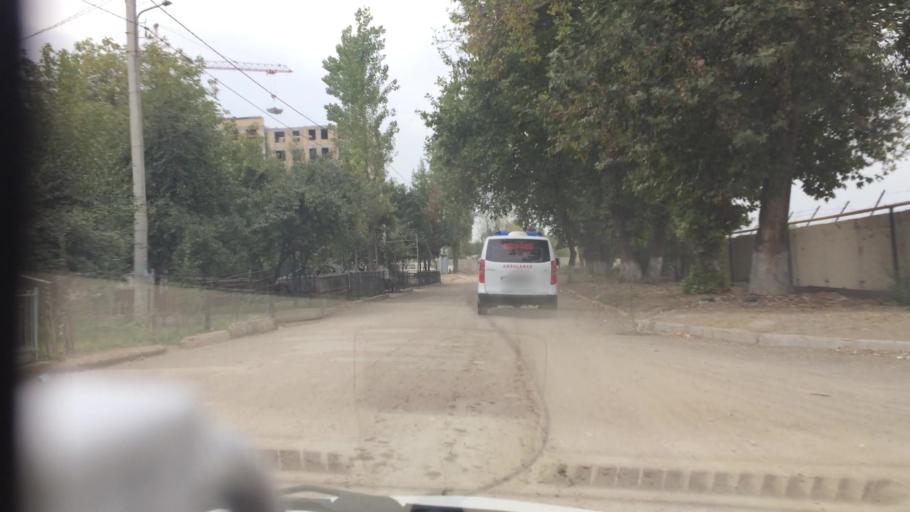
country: UZ
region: Toshkent
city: Salor
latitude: 41.3072
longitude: 69.3364
